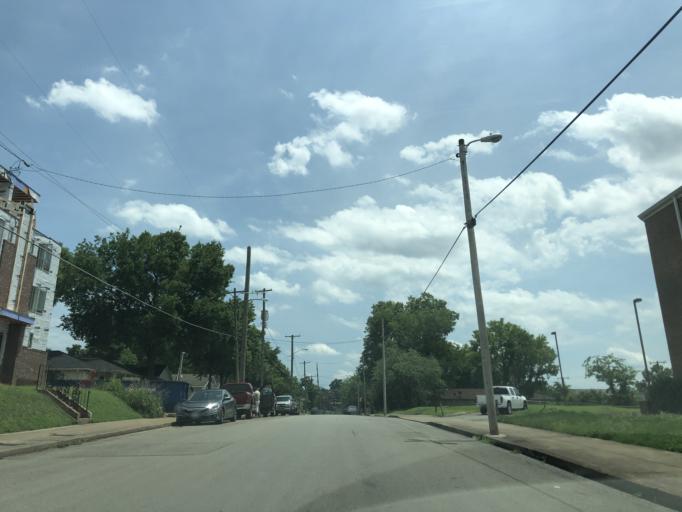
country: US
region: Tennessee
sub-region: Davidson County
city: Nashville
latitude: 36.1787
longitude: -86.7593
